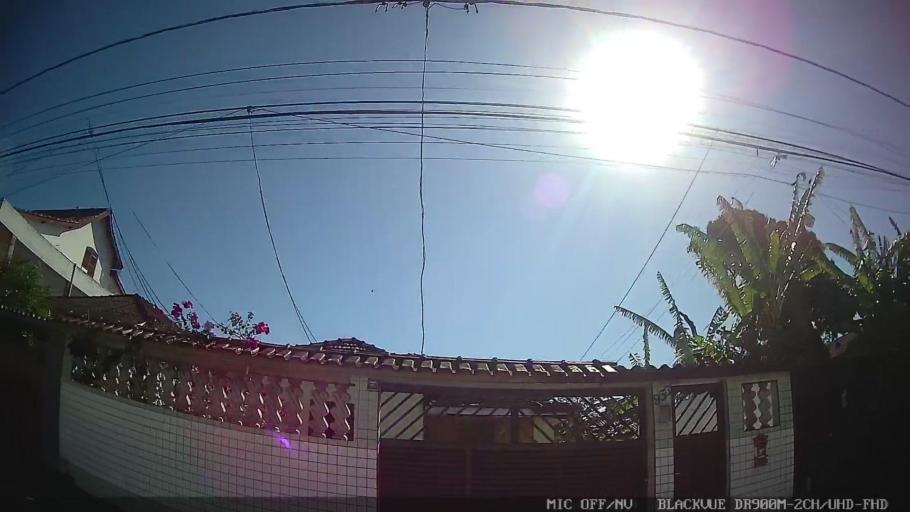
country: BR
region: Sao Paulo
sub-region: Santos
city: Santos
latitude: -23.9425
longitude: -46.2894
